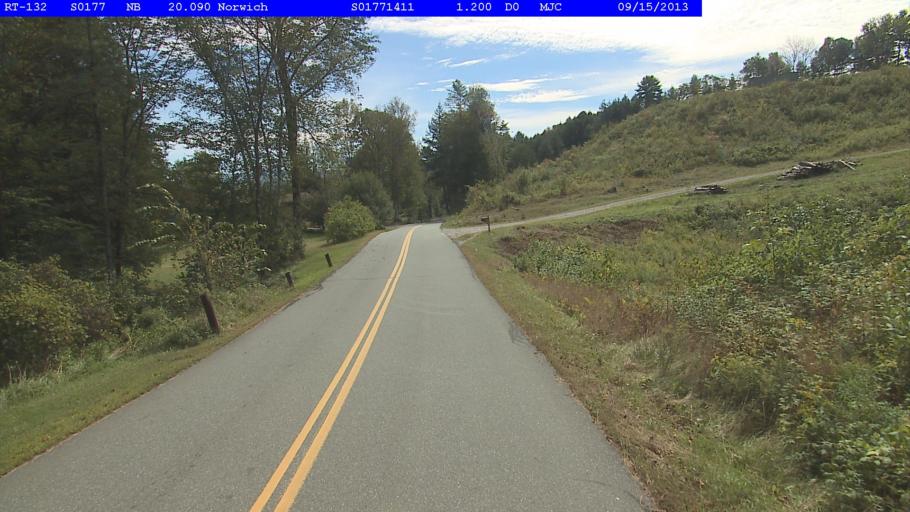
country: US
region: New Hampshire
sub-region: Grafton County
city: Hanover
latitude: 43.7712
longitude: -72.2530
